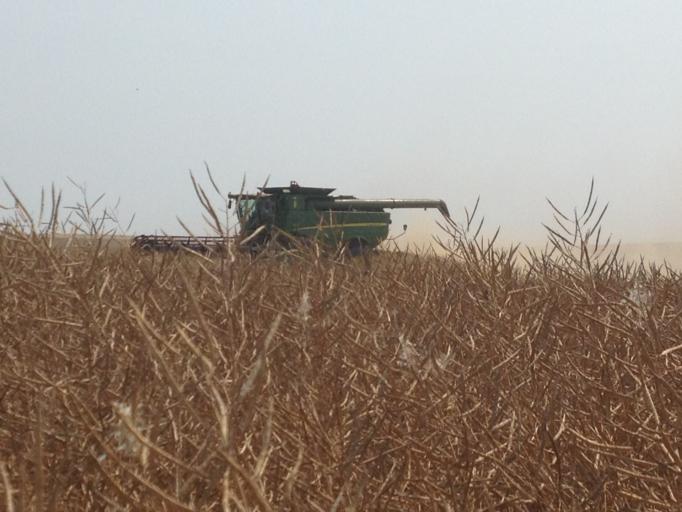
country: US
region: North Dakota
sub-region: Hettinger County
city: Mott
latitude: 46.3697
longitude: -102.5553
